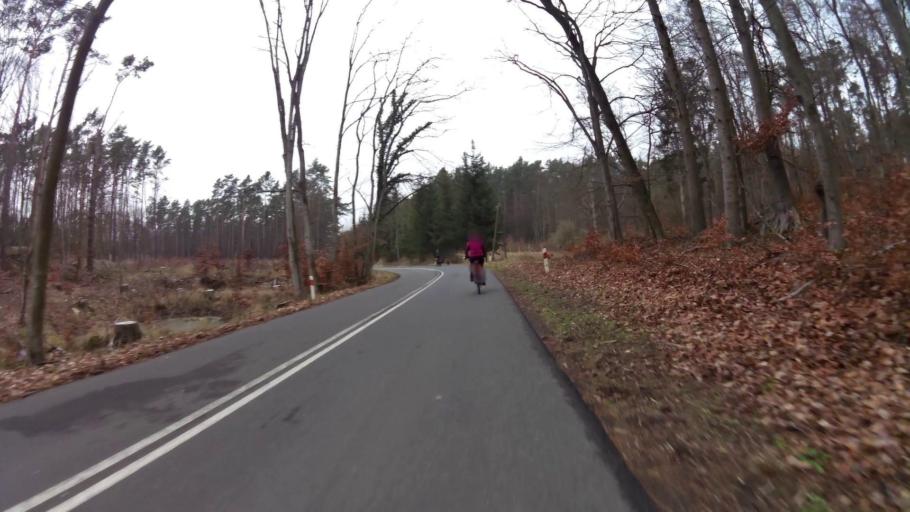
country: PL
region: West Pomeranian Voivodeship
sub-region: Powiat gryfinski
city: Cedynia
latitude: 52.9215
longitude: 14.2030
